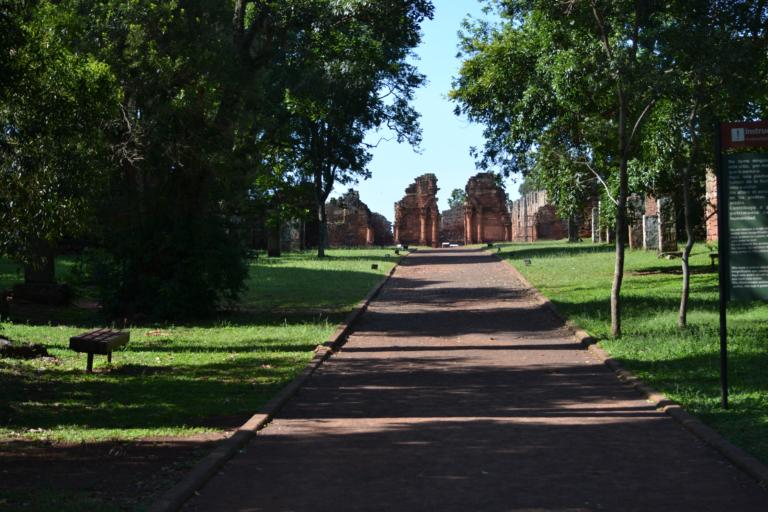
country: AR
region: Misiones
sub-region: Departamento de San Ignacio
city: San Ignacio
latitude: -27.2532
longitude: -55.5315
